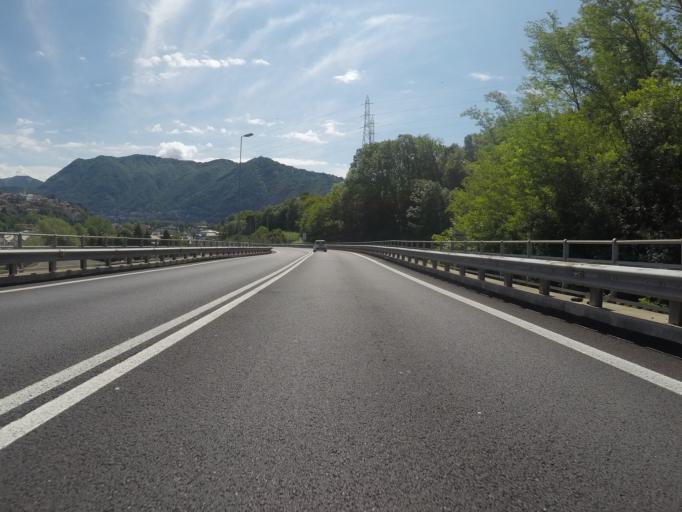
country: IT
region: Lombardy
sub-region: Provincia di Como
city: Maslianico
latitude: 45.8383
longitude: 9.0503
